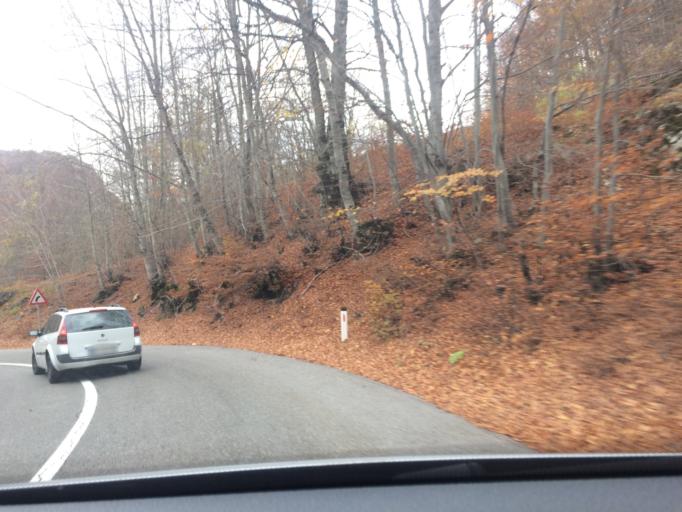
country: ME
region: Opstina Savnik
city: Savnik
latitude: 42.9493
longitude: 19.0932
